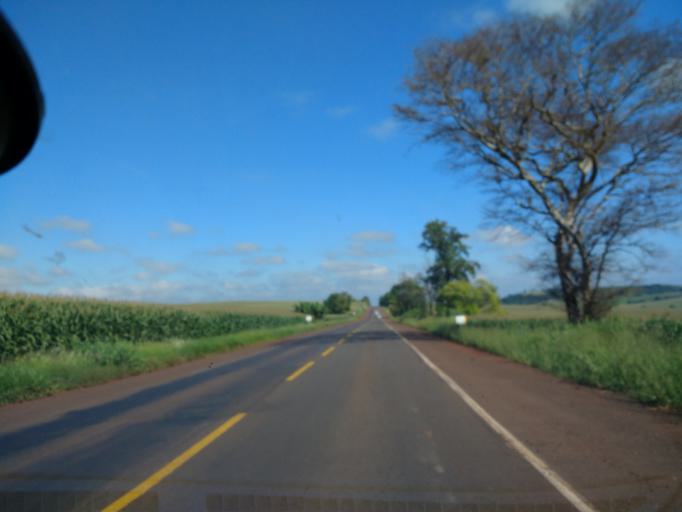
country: BR
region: Parana
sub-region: Paicandu
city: Paicandu
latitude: -23.5070
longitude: -52.1629
